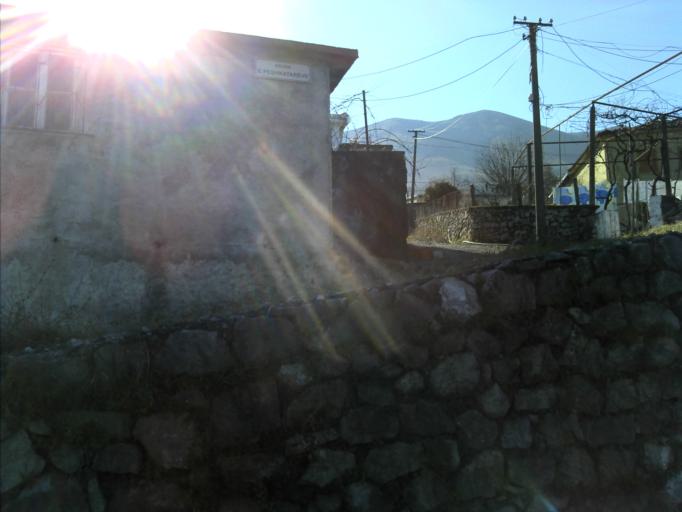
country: AL
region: Shkoder
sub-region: Rrethi i Shkodres
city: Berdica e Madhe
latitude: 42.0598
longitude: 19.4520
